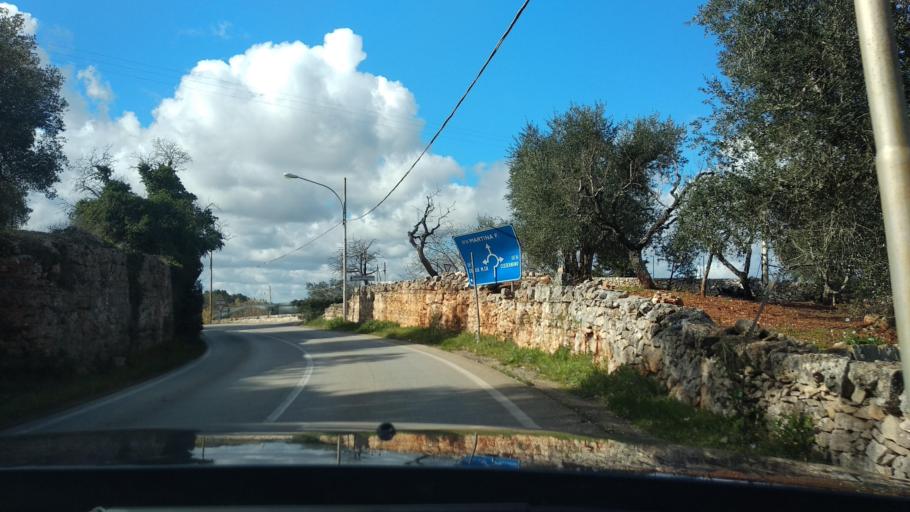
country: IT
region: Apulia
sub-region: Provincia di Brindisi
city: Casalini
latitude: 40.7012
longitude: 17.4942
